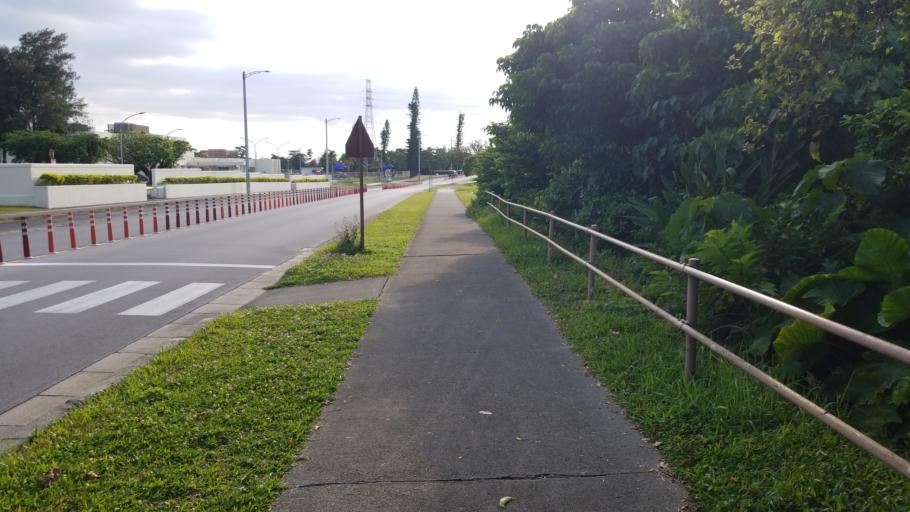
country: JP
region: Okinawa
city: Okinawa
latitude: 26.3384
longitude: 127.7853
